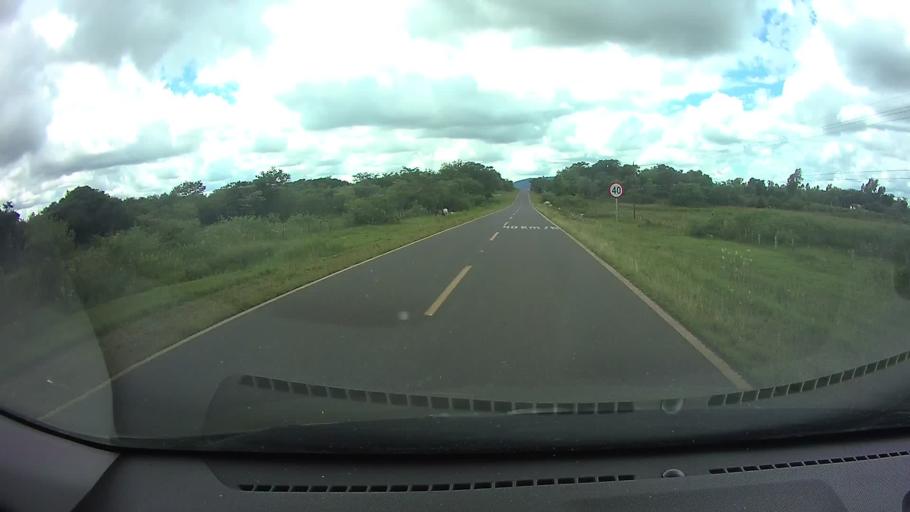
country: PY
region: Paraguari
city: Ybycui
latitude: -25.9132
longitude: -57.0429
